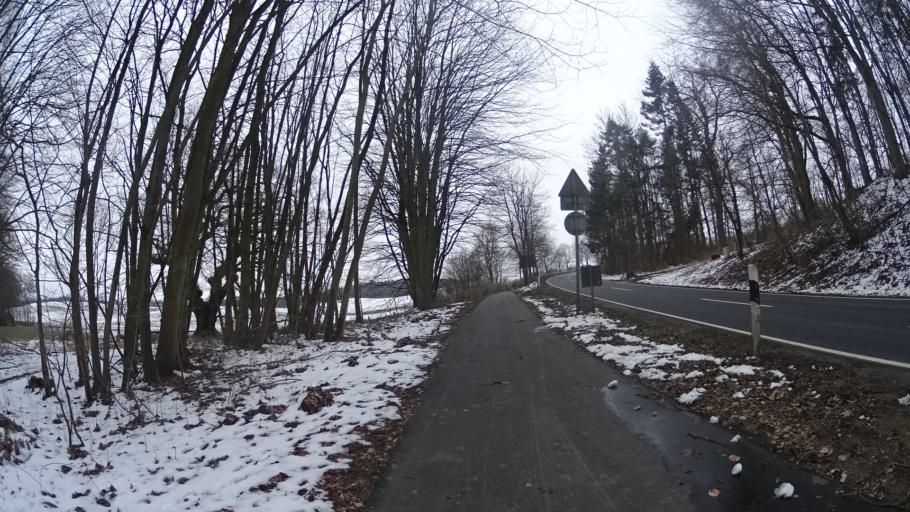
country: DE
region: Schleswig-Holstein
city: Panker
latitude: 54.3257
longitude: 10.5704
